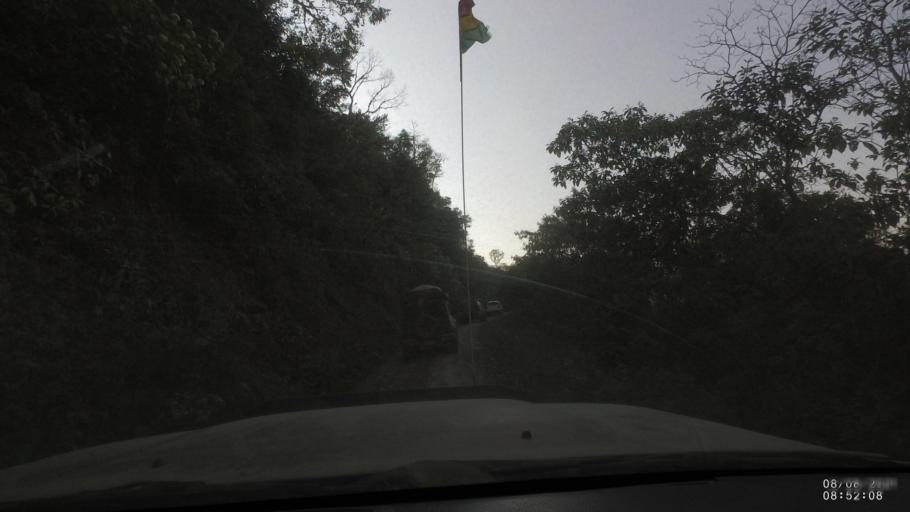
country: BO
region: La Paz
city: Quime
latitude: -16.5394
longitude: -66.7597
